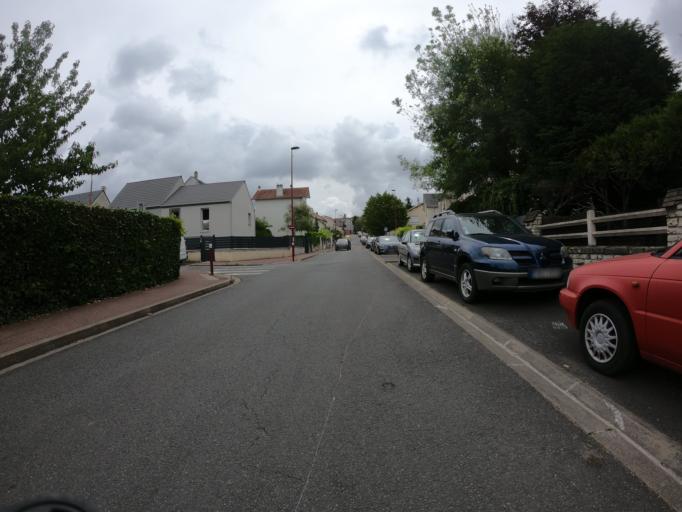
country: FR
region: Ile-de-France
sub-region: Departement du Val-de-Marne
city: Fresnes
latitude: 48.7562
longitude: 2.3189
